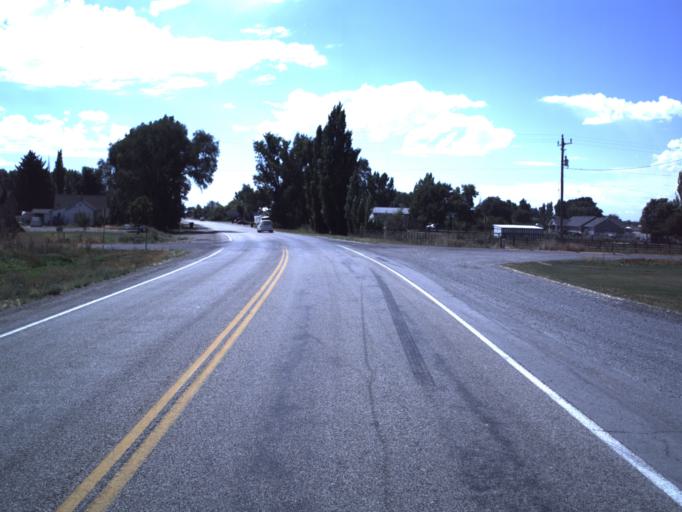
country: US
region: Utah
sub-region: Box Elder County
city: Garland
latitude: 41.7929
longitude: -112.1494
